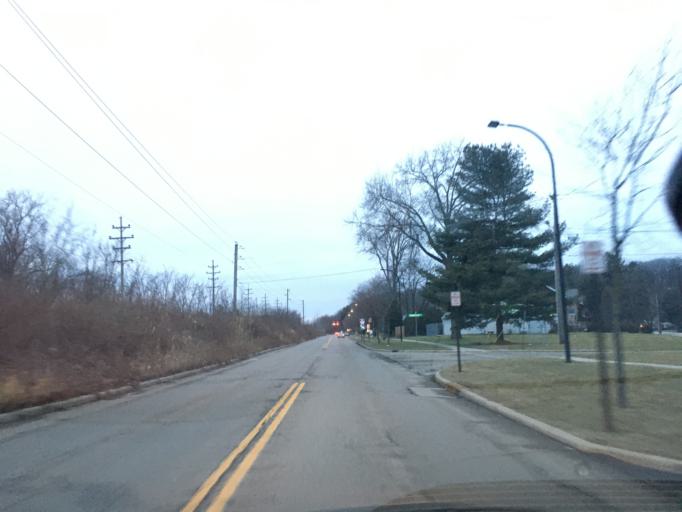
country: US
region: Ohio
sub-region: Summit County
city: Fairlawn
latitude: 41.1113
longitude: -81.5811
